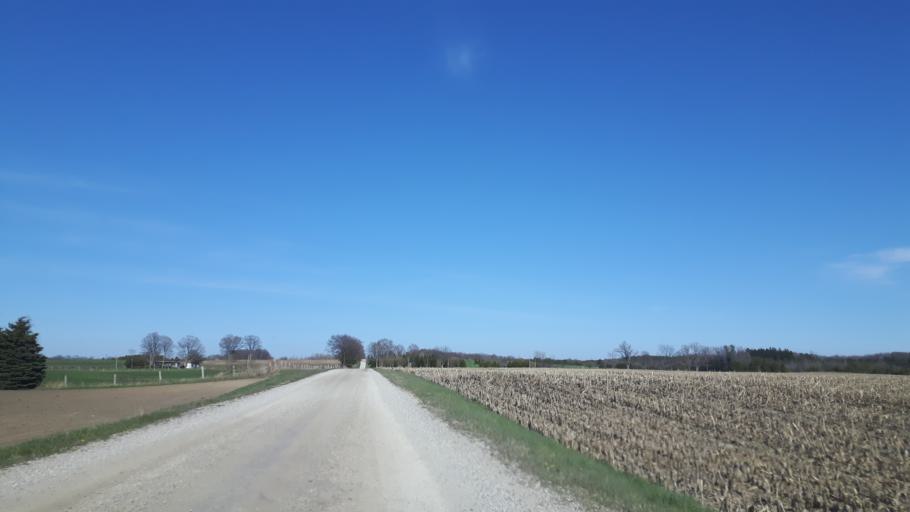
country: CA
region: Ontario
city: Goderich
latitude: 43.6613
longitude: -81.6909
